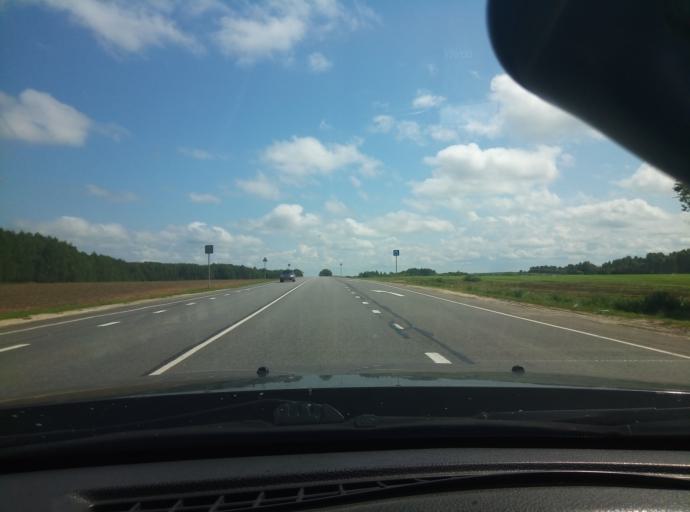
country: RU
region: Tula
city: Khanino
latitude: 54.4158
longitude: 36.5315
